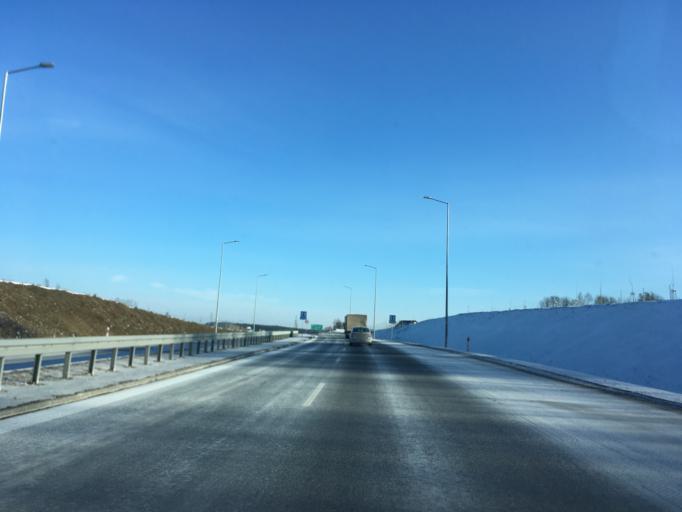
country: PL
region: Pomeranian Voivodeship
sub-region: Powiat koscierski
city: Koscierzyna
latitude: 54.1090
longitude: 17.9592
